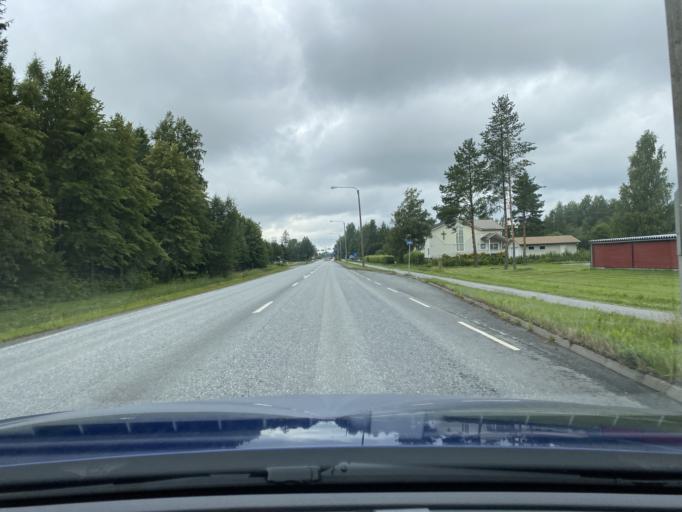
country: FI
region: Ostrobothnia
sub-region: Kyroenmaa
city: Laihia
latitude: 62.9754
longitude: 22.0189
